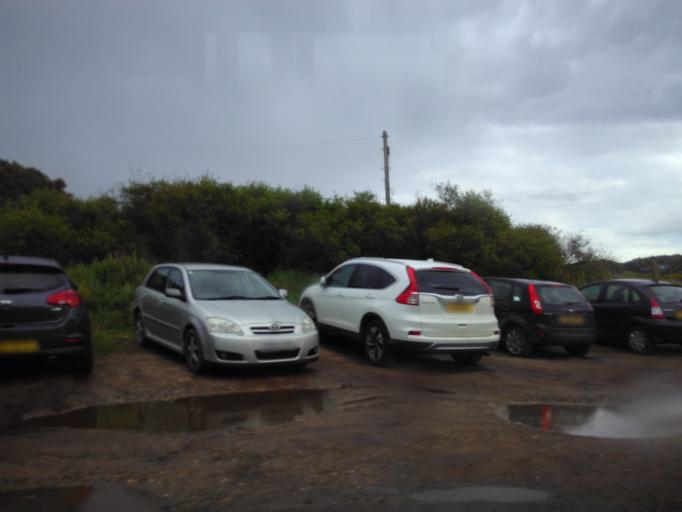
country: GB
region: England
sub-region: Norfolk
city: Briston
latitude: 52.9547
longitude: 1.0668
